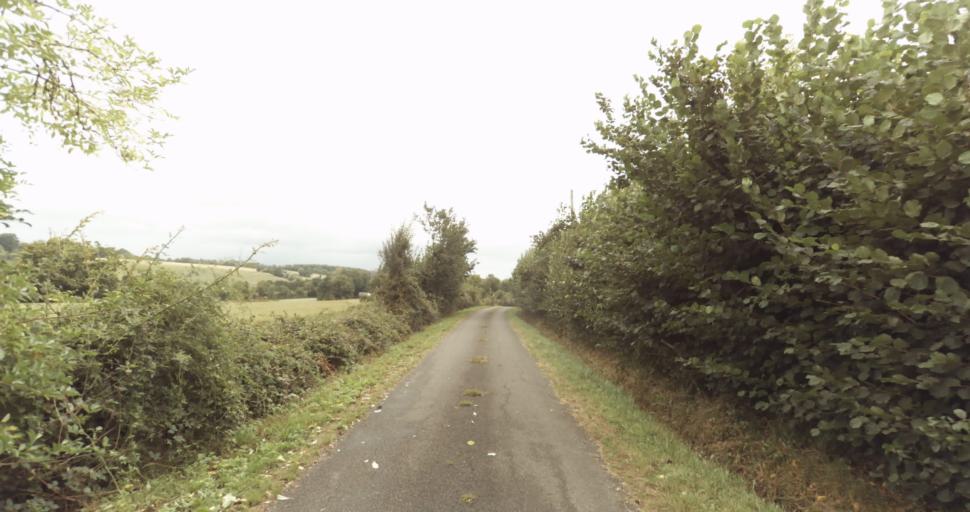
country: FR
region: Lower Normandy
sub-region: Departement de l'Orne
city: Sainte-Gauburge-Sainte-Colombe
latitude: 48.7010
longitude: 0.4477
